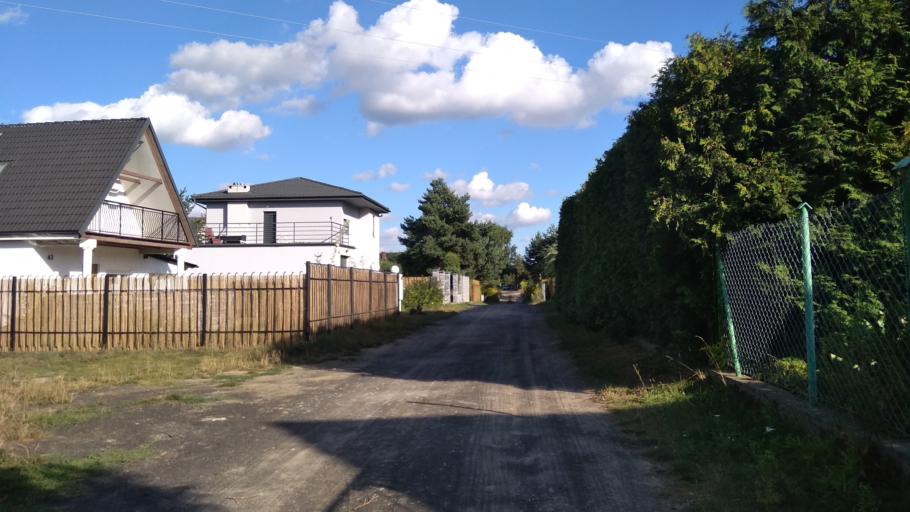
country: PL
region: Kujawsko-Pomorskie
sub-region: Powiat bydgoski
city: Osielsko
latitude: 53.2305
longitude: 18.1206
